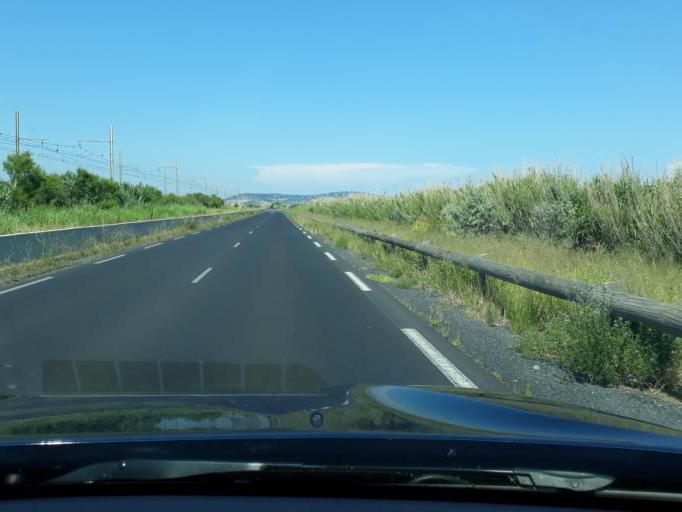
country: FR
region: Languedoc-Roussillon
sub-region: Departement de l'Herault
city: Meze
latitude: 43.3638
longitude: 3.6093
